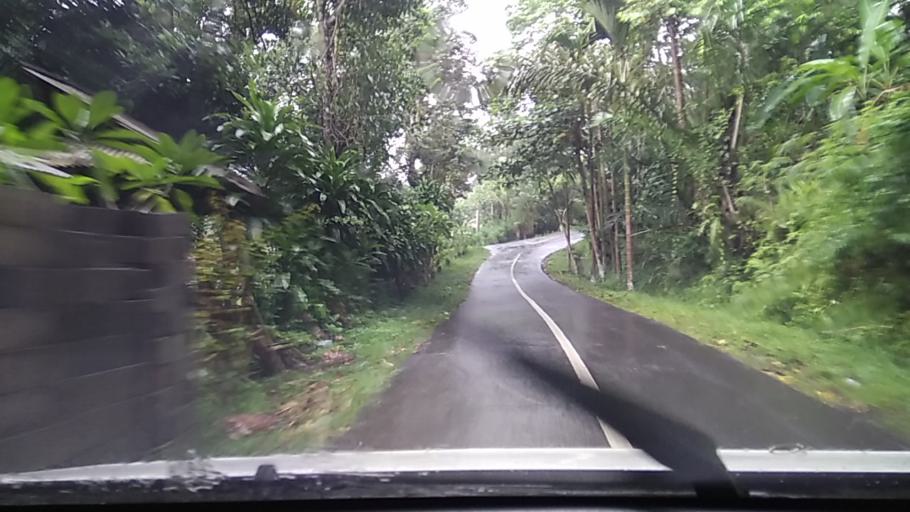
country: ID
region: Bali
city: Tiyingtali Kelod
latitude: -8.4098
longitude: 115.6240
